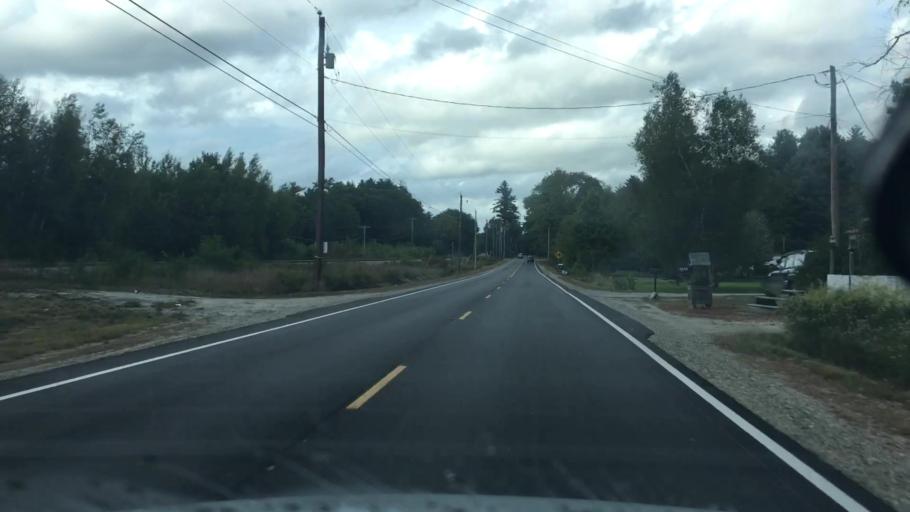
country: US
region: New Hampshire
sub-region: Carroll County
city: Sanbornville
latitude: 43.5419
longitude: -71.0273
